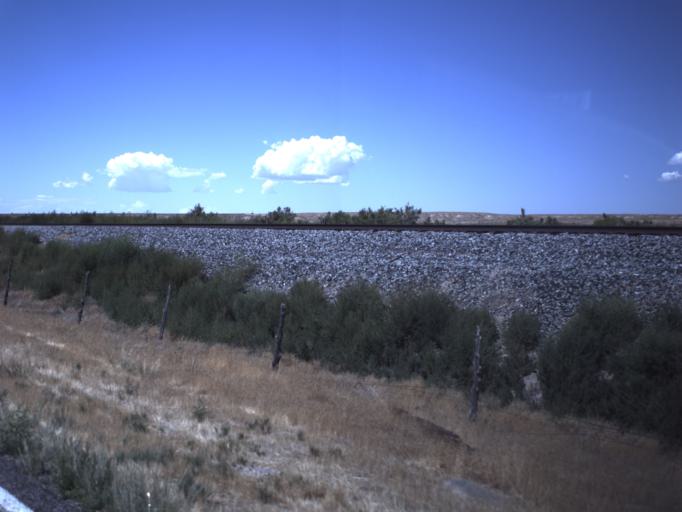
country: US
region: Utah
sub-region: Millard County
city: Delta
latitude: 39.5332
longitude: -112.3228
